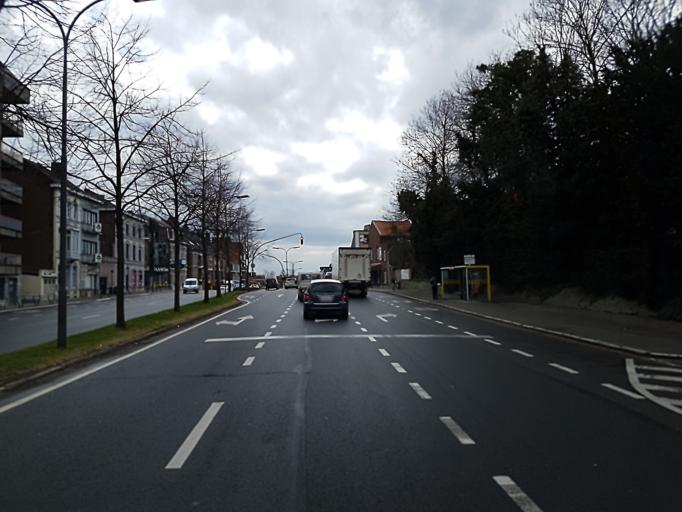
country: BE
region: Flanders
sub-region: Provincie Limburg
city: Tongeren
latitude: 50.7809
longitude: 5.4601
